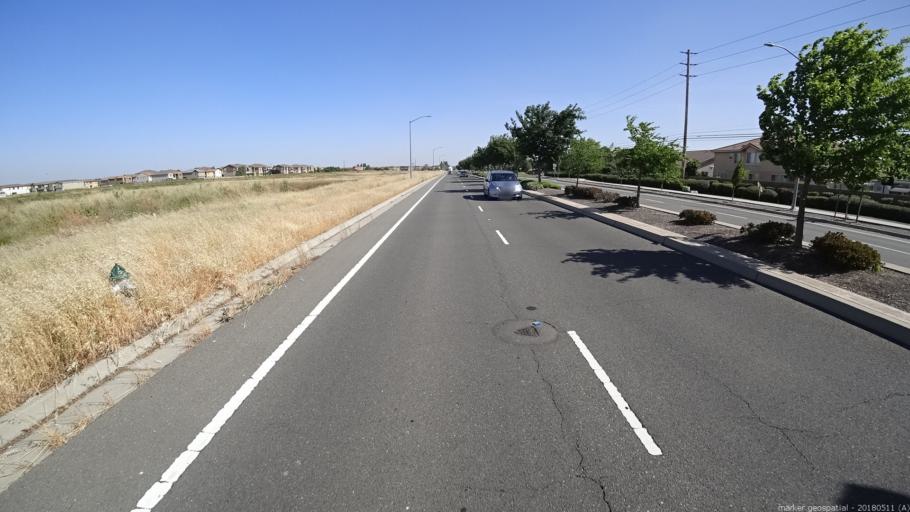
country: US
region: California
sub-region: Yolo County
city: West Sacramento
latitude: 38.6512
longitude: -121.5399
